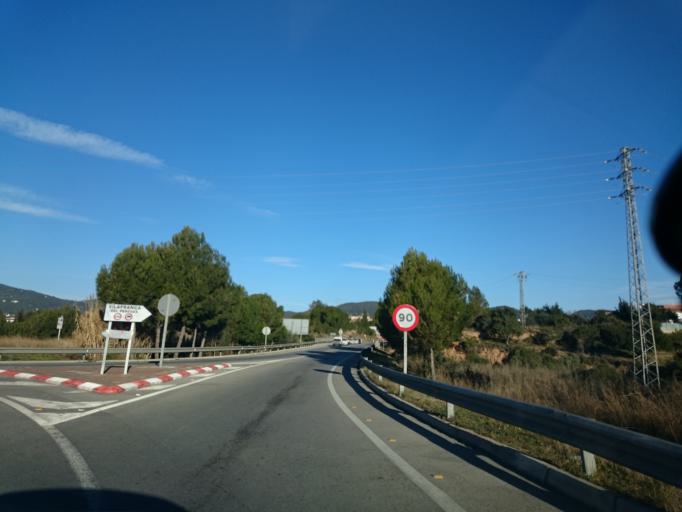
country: ES
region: Catalonia
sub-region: Provincia de Barcelona
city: Sant Pere de Ribes
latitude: 41.2528
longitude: 1.7839
